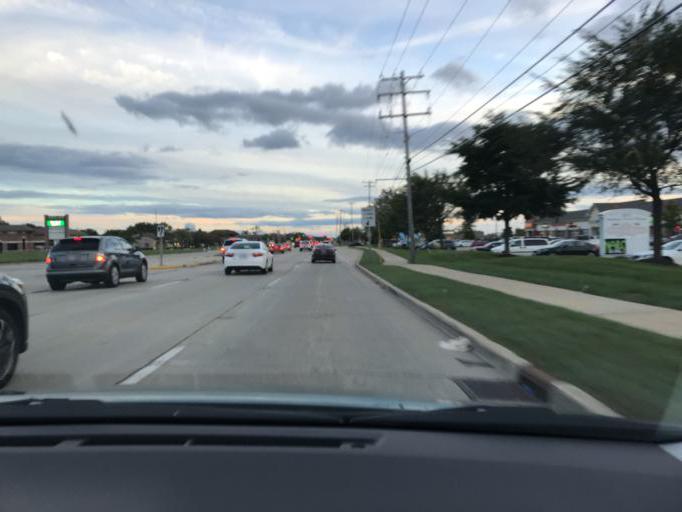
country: US
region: Wisconsin
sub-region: Kenosha County
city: Pleasant Prairie
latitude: 42.5774
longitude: -87.8854
